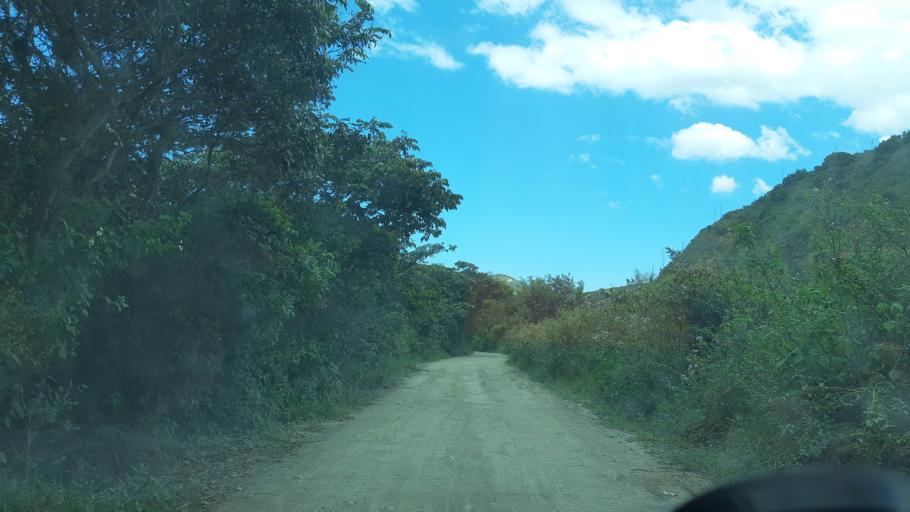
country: CO
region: Boyaca
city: Villa de Leiva
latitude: 5.6832
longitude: -73.5687
